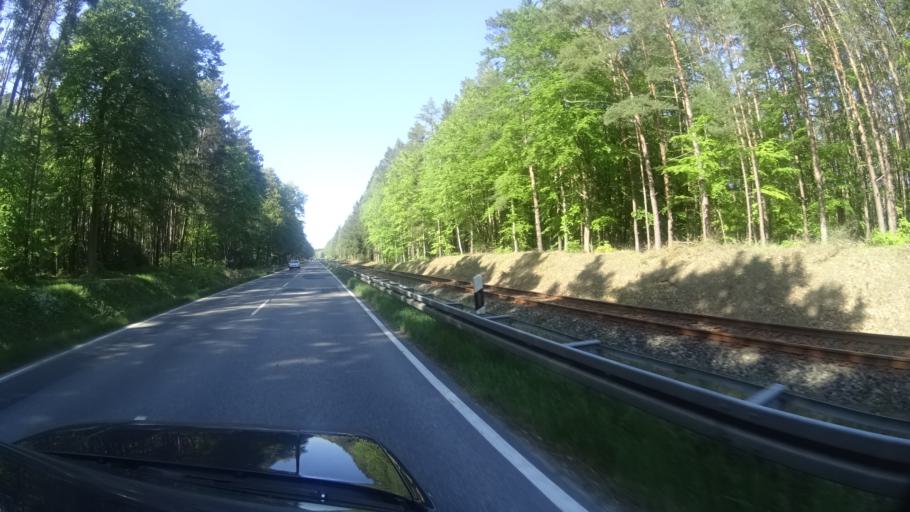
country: DE
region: Mecklenburg-Vorpommern
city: Seeheilbad Graal-Muritz
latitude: 54.2315
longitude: 12.2247
